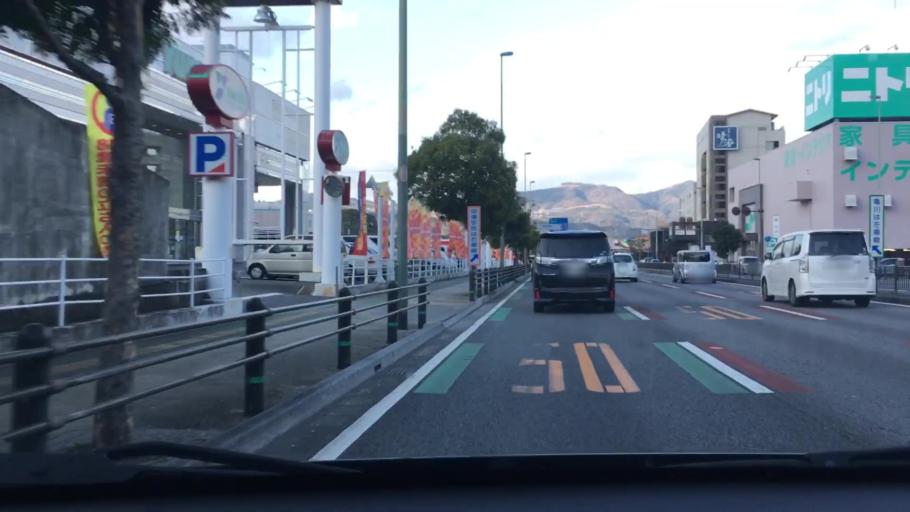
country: JP
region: Oita
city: Beppu
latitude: 33.3153
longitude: 131.5002
